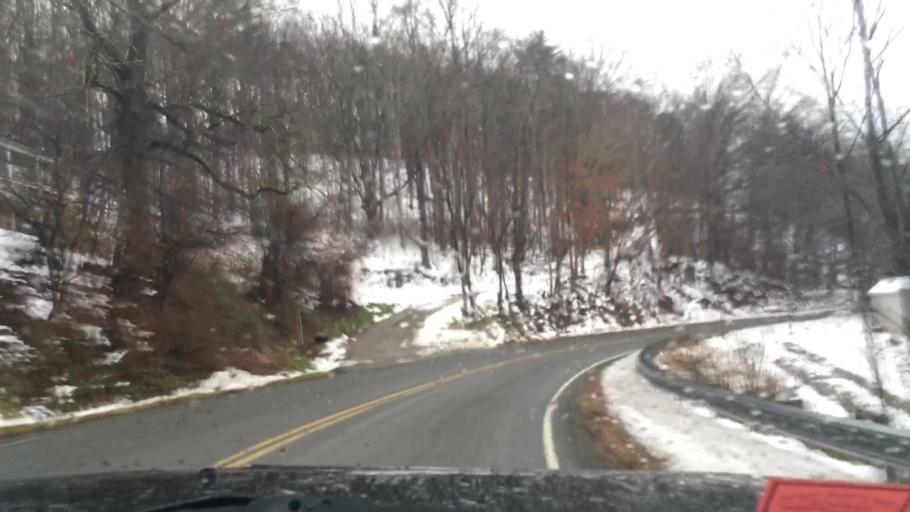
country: US
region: Virginia
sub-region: Pulaski County
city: Dublin
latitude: 37.0090
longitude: -80.6863
